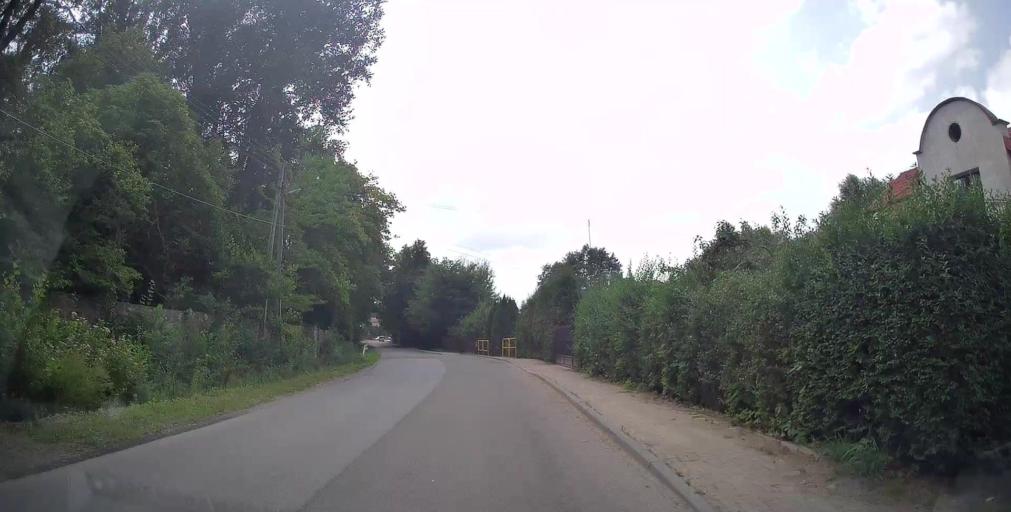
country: PL
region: Masovian Voivodeship
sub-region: Powiat bialobrzeski
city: Sucha
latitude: 51.6219
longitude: 20.9514
